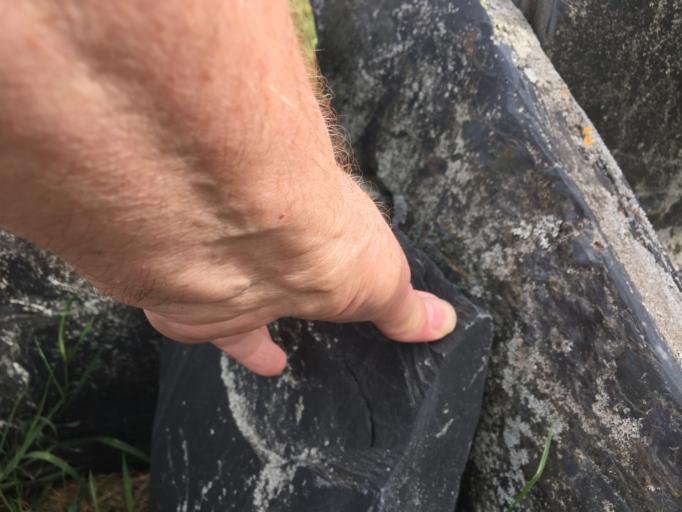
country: SE
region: OErebro
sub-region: Hallefors Kommun
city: Haellefors
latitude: 59.7061
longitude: 14.5467
